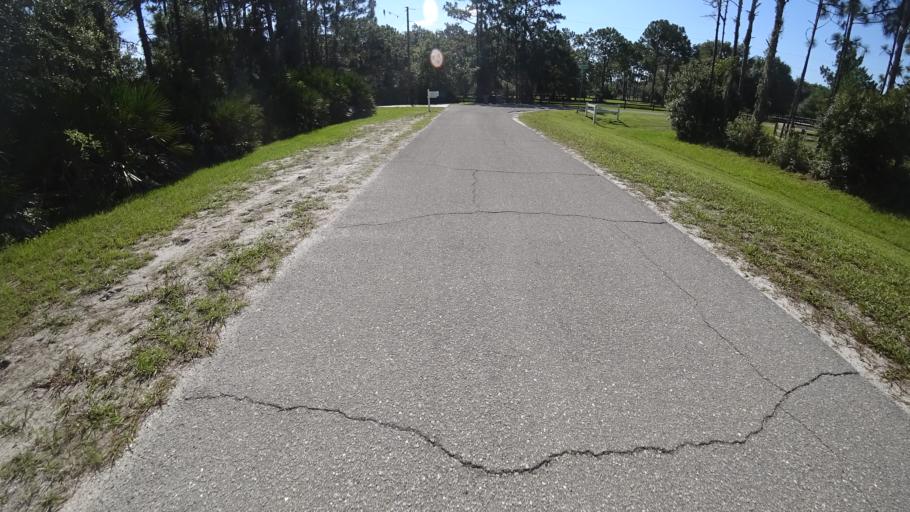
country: US
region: Florida
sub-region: Sarasota County
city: The Meadows
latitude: 27.4167
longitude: -82.3310
